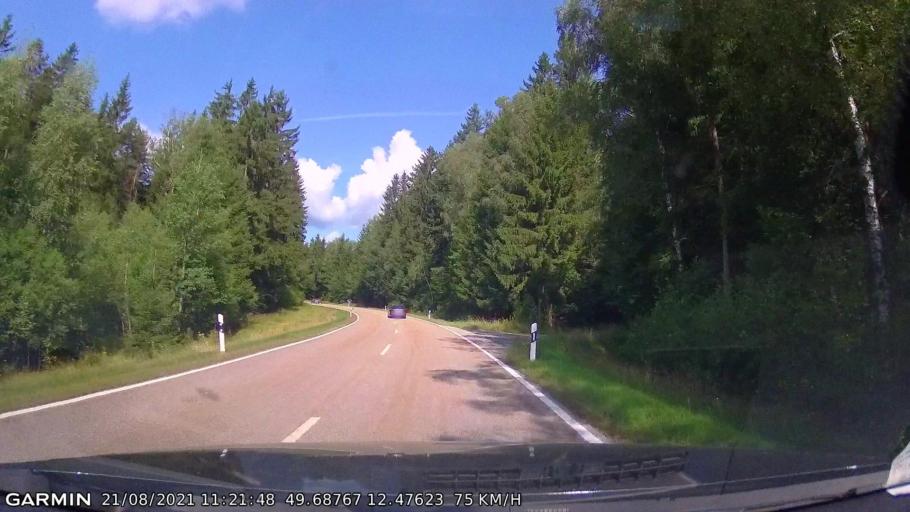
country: DE
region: Bavaria
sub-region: Upper Palatinate
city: Waidhaus
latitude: 49.6877
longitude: 12.4762
